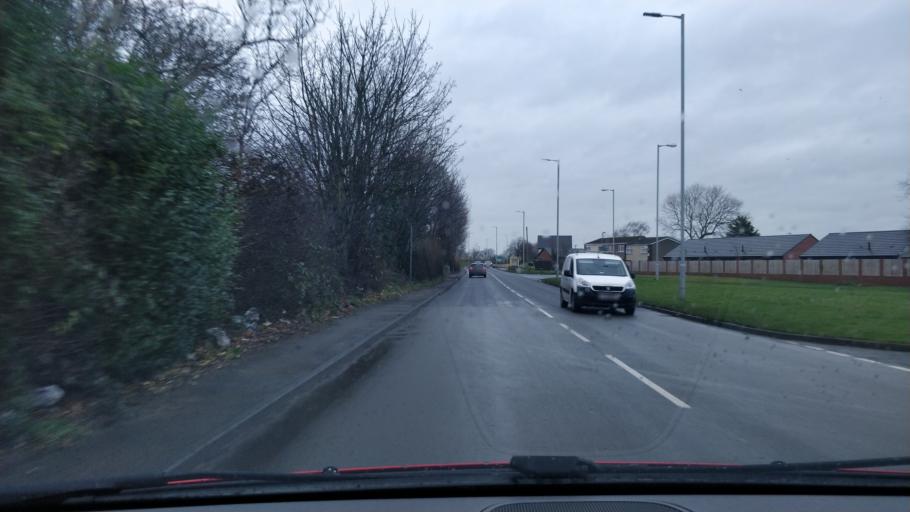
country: GB
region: England
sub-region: Sefton
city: Thornton
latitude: 53.4926
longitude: -2.9866
